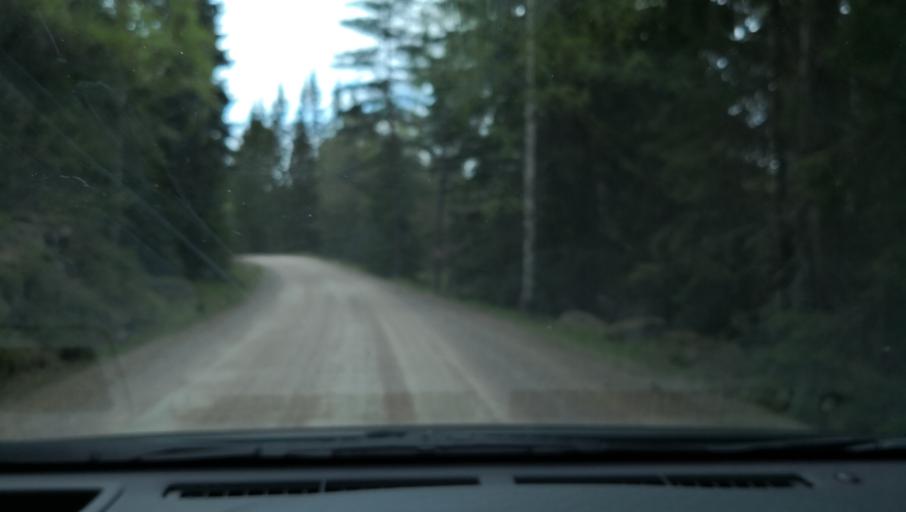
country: SE
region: Vaestmanland
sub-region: Fagersta Kommun
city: Fagersta
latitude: 60.1104
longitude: 15.7987
